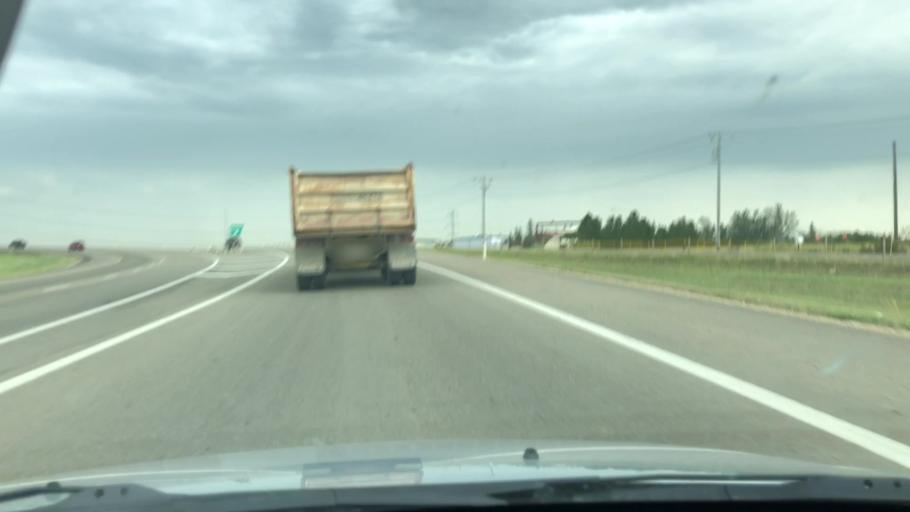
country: CA
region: Alberta
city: Sherwood Park
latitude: 53.5123
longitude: -113.3492
